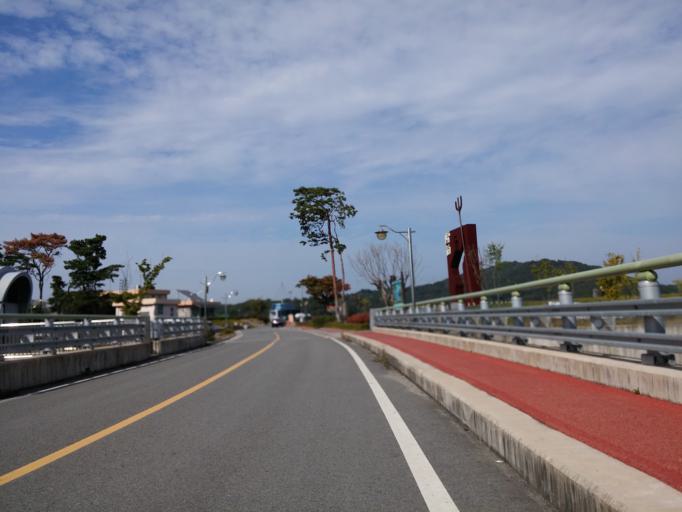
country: KR
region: Chungcheongnam-do
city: Yonmu
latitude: 36.1751
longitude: 127.1490
